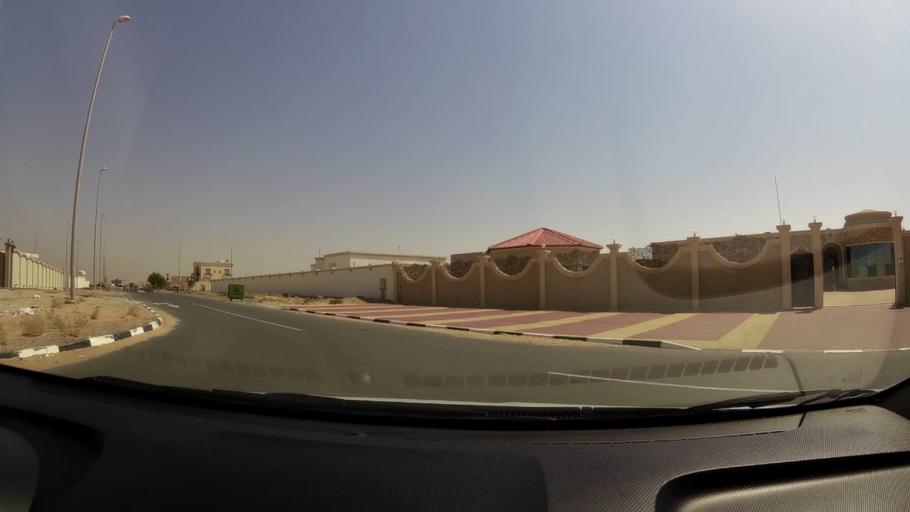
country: AE
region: Umm al Qaywayn
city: Umm al Qaywayn
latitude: 25.4880
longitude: 55.6028
